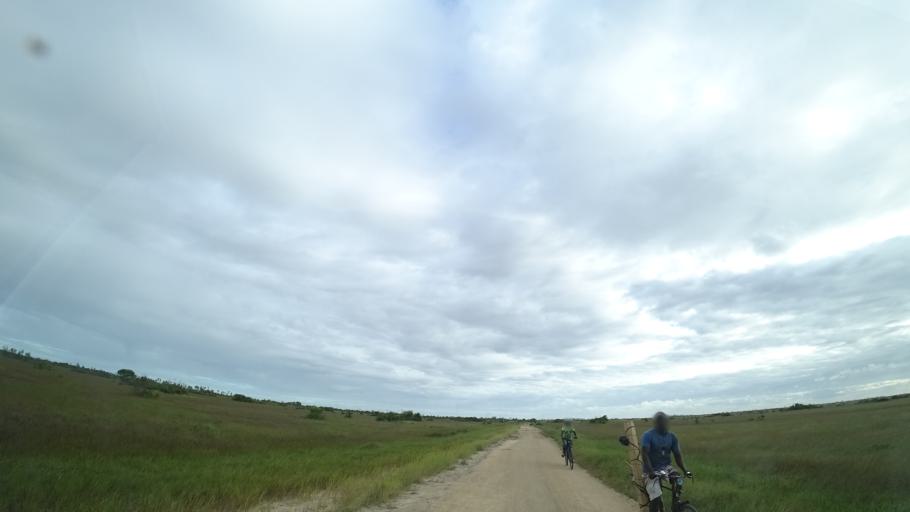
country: MZ
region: Sofala
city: Beira
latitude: -19.7030
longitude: 35.0231
